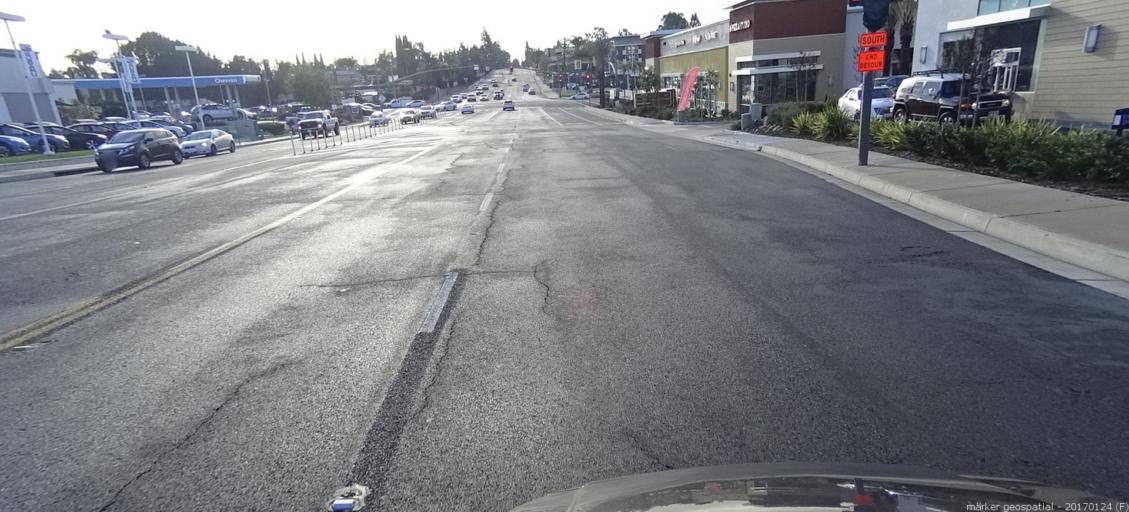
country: US
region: California
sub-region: Orange County
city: Laguna Hills
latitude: 33.6302
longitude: -117.7179
